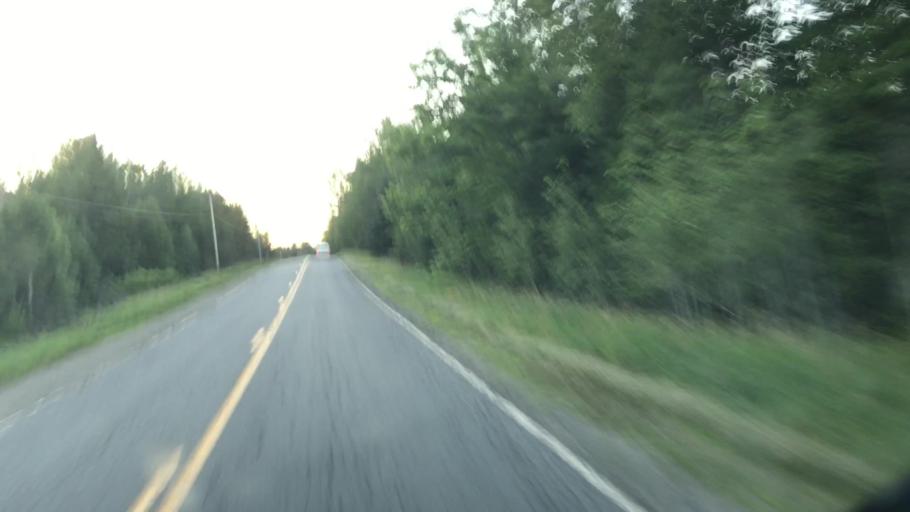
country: US
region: Maine
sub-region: Penobscot County
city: Medway
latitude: 45.6035
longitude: -68.2522
